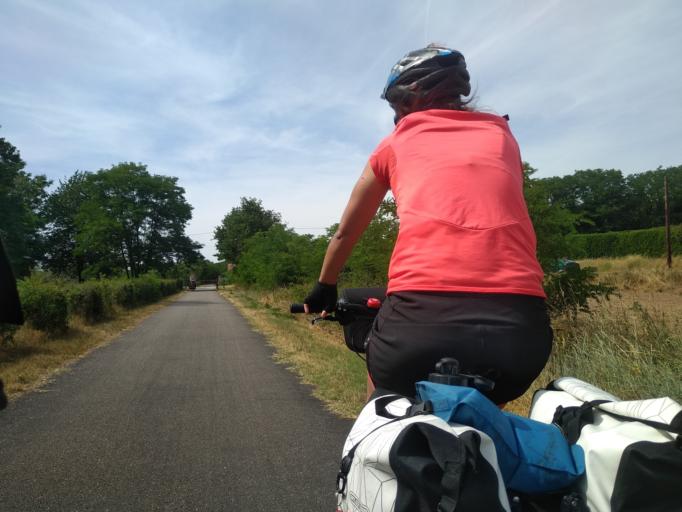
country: FR
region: Auvergne
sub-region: Departement de l'Allier
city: Diou
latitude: 46.5406
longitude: 3.7497
